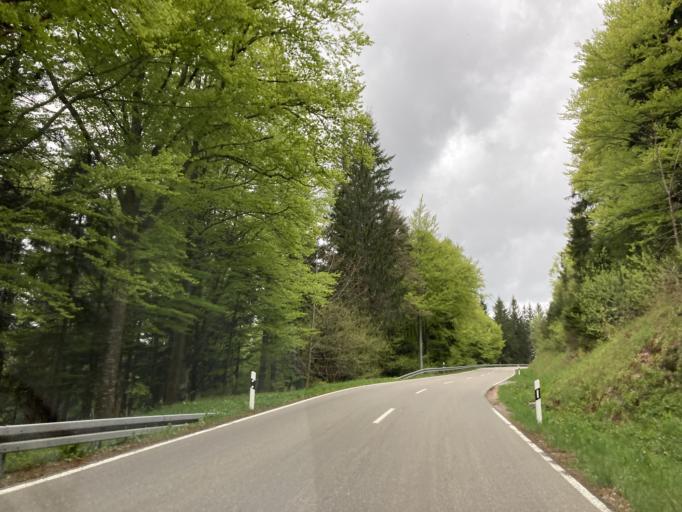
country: DE
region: Baden-Wuerttemberg
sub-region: Freiburg Region
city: Schonach im Schwarzwald
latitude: 48.1323
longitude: 8.1612
